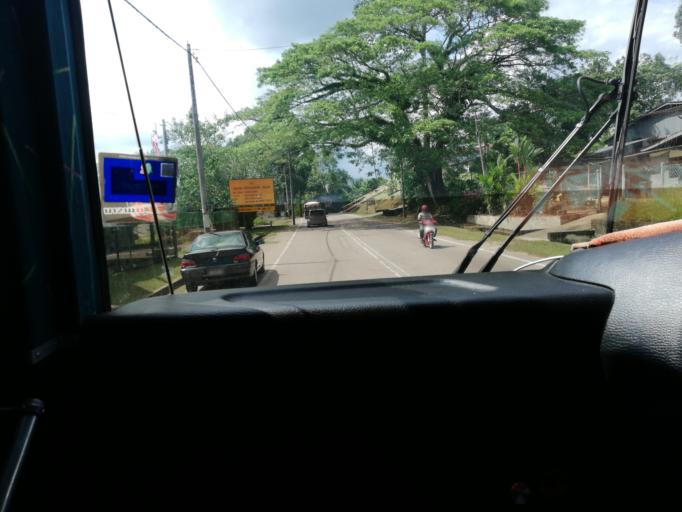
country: MY
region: Penang
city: Nibong Tebal
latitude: 5.2155
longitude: 100.6111
